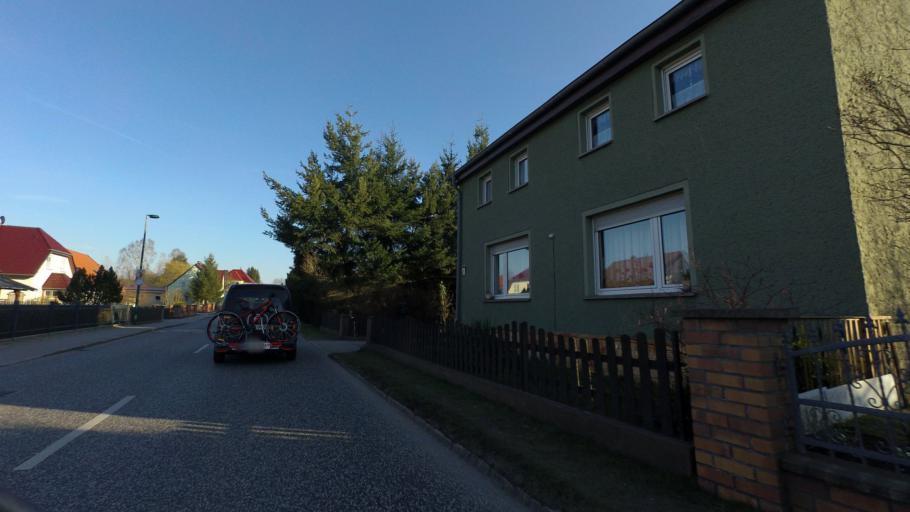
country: DE
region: Brandenburg
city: Britz
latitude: 52.8867
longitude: 13.8117
